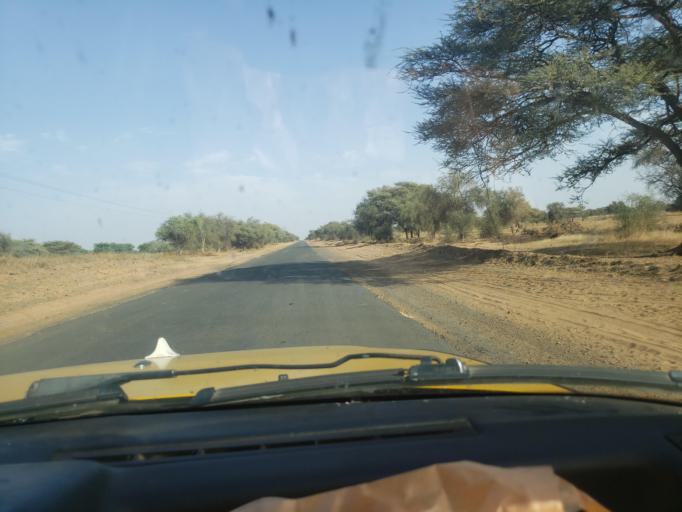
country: SN
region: Louga
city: Louga
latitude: 15.5052
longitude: -15.9585
